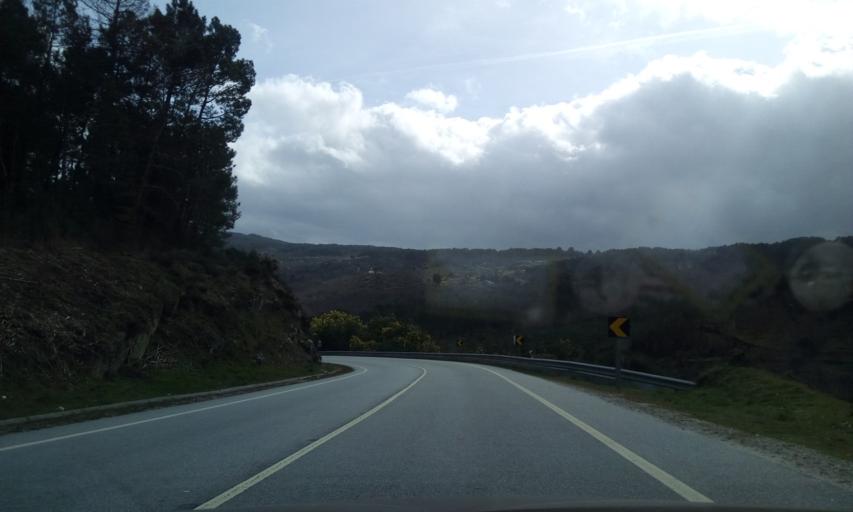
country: PT
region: Viseu
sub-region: Mangualde
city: Mangualde
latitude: 40.6475
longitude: -7.7324
